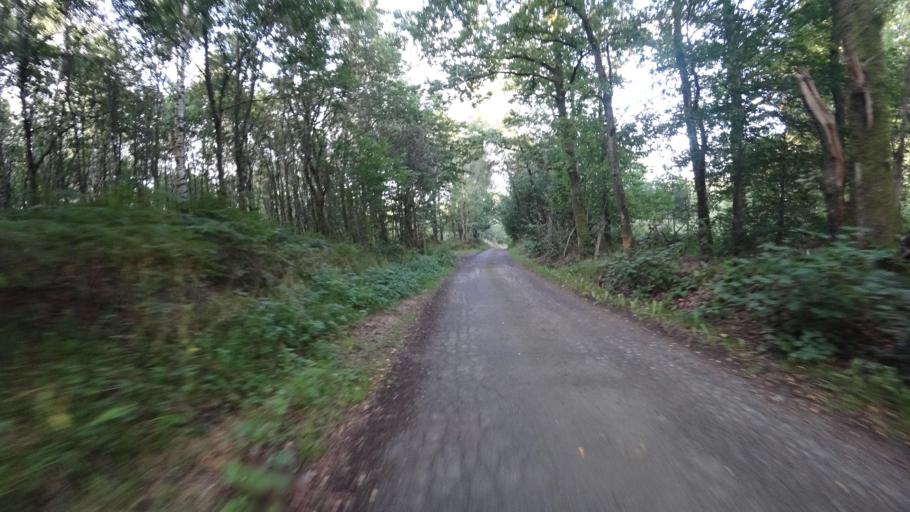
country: BE
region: Wallonia
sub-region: Province du Luxembourg
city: Neufchateau
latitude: 49.8711
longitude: 5.3769
